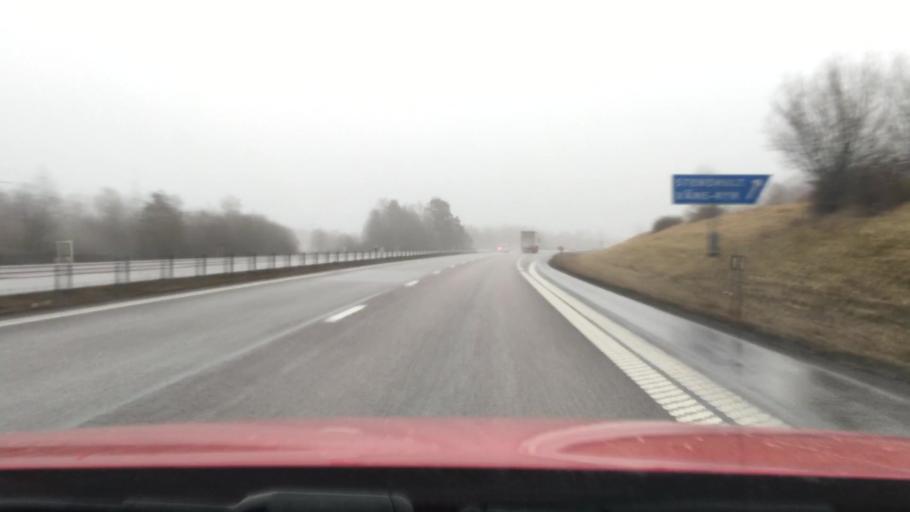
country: SE
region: Vaestra Goetaland
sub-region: Trollhattan
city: Sjuntorp
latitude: 58.3344
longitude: 12.1201
